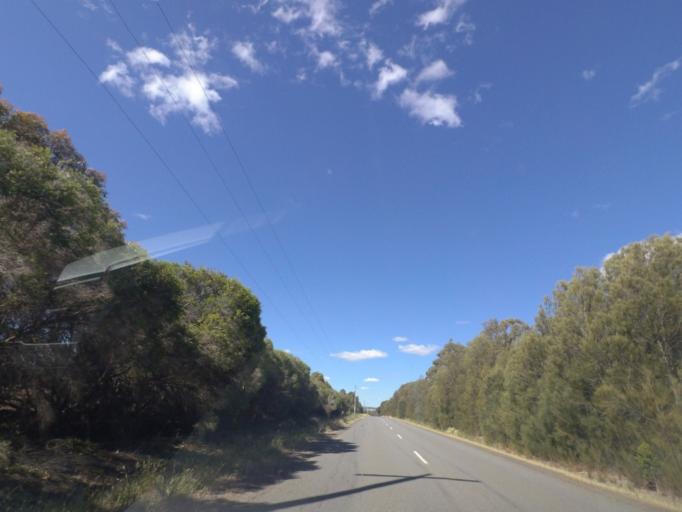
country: AU
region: Victoria
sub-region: Hume
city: Craigieburn
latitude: -37.4182
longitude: 144.8800
